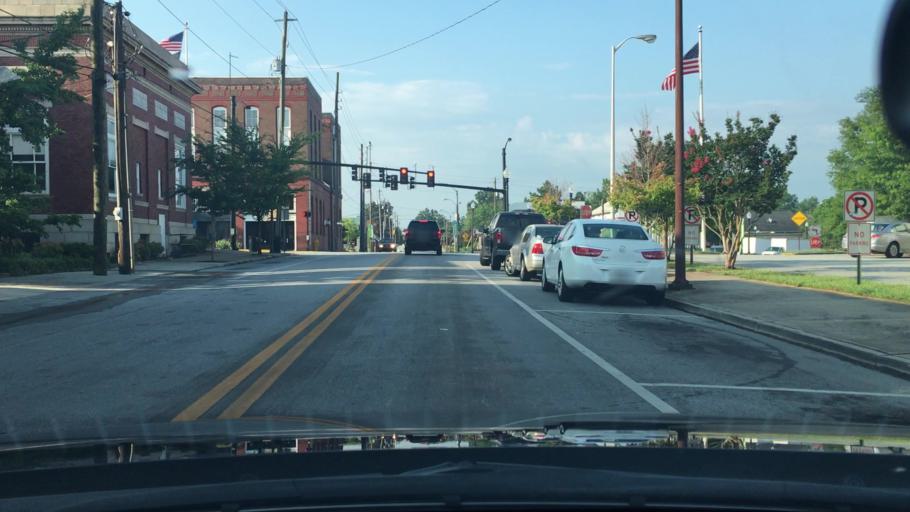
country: US
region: Georgia
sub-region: Spalding County
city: Griffin
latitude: 33.2493
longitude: -84.2655
